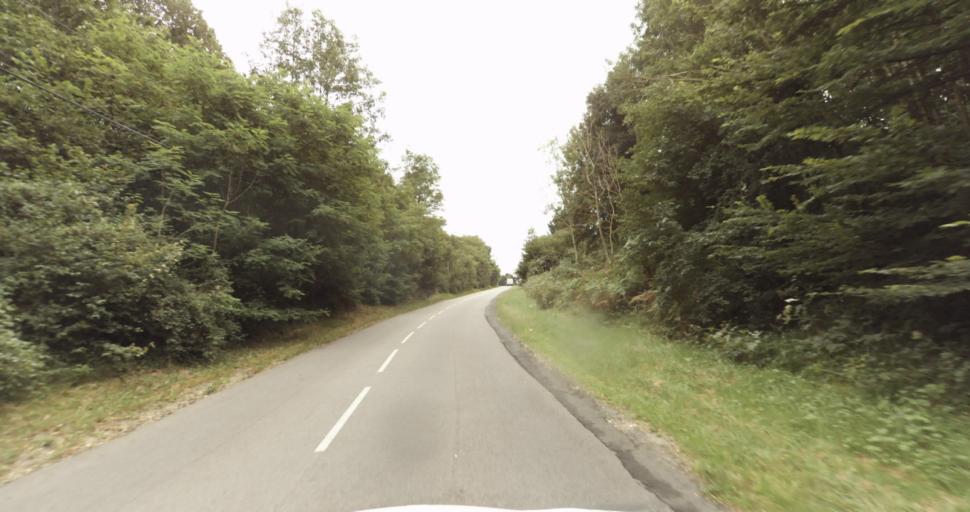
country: FR
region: Haute-Normandie
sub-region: Departement de l'Eure
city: Gravigny
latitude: 49.0422
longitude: 1.1728
